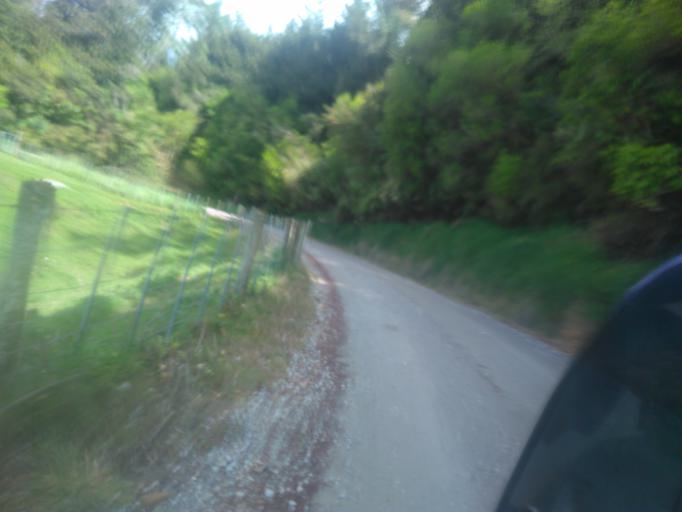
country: NZ
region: Hawke's Bay
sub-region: Wairoa District
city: Wairoa
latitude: -38.7755
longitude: 177.6080
